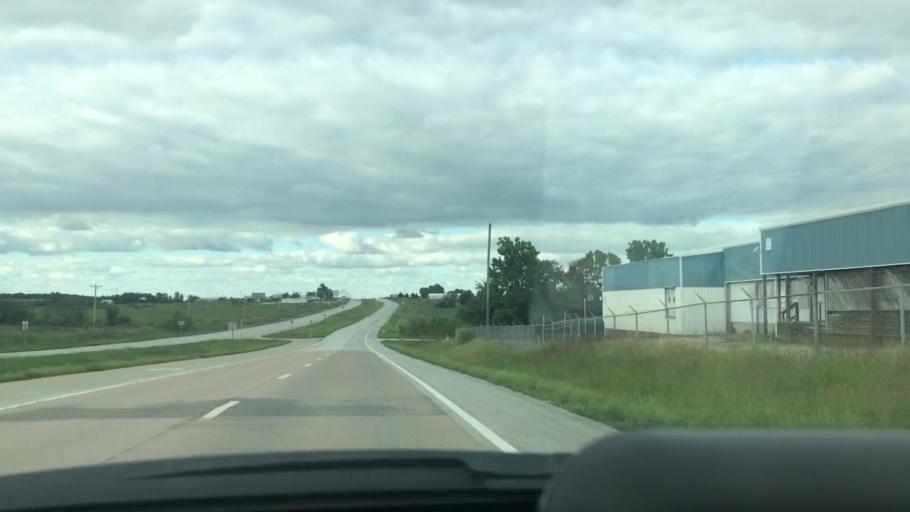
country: US
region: Missouri
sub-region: Benton County
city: Lincoln
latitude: 38.3322
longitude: -93.3413
